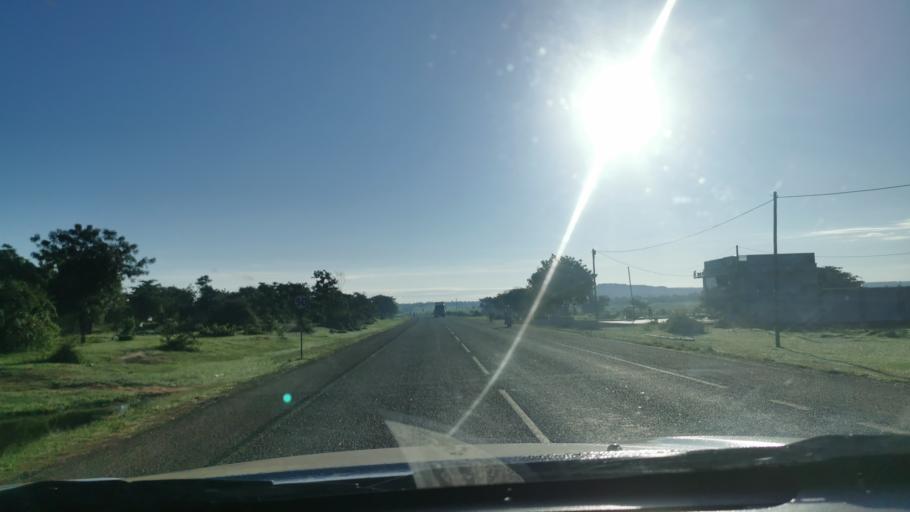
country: TZ
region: Shinyanga
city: Kahama
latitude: -3.8391
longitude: 32.6416
